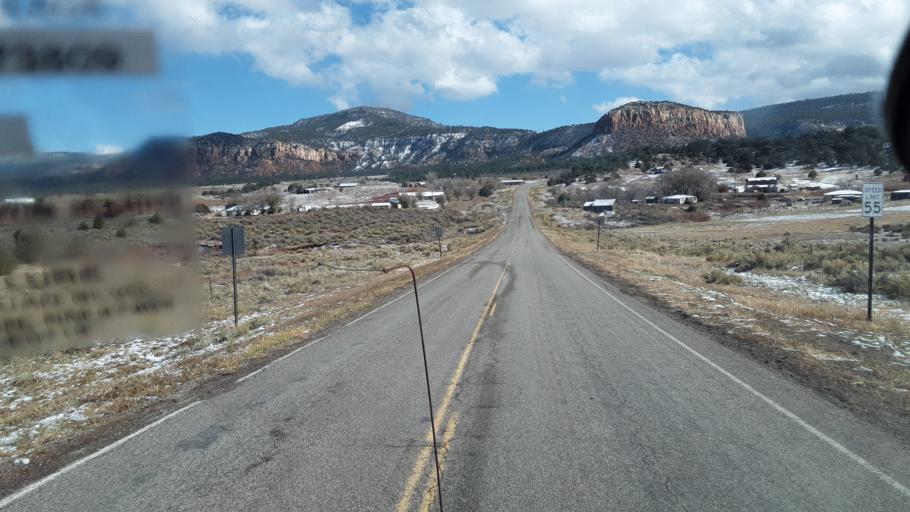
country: US
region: New Mexico
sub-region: Rio Arriba County
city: Santa Teresa
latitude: 36.2297
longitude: -106.8129
